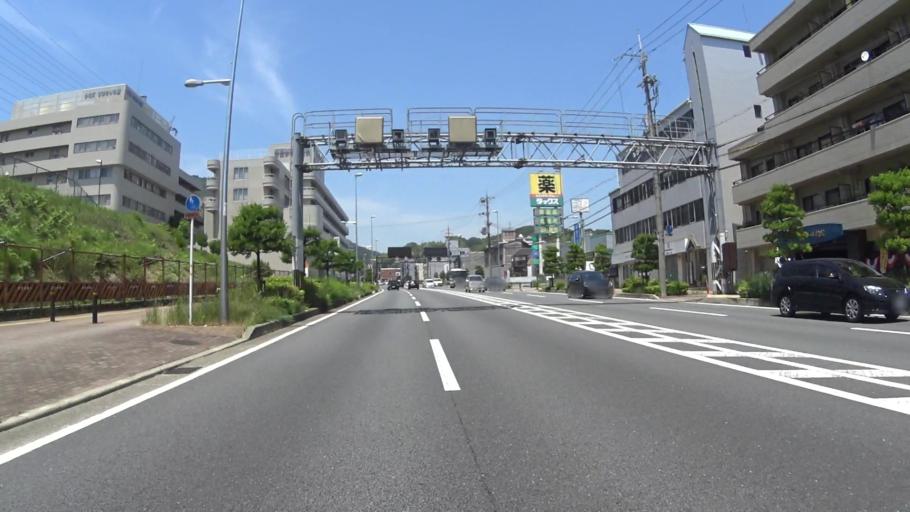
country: JP
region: Kyoto
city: Muko
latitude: 34.9751
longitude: 135.6664
